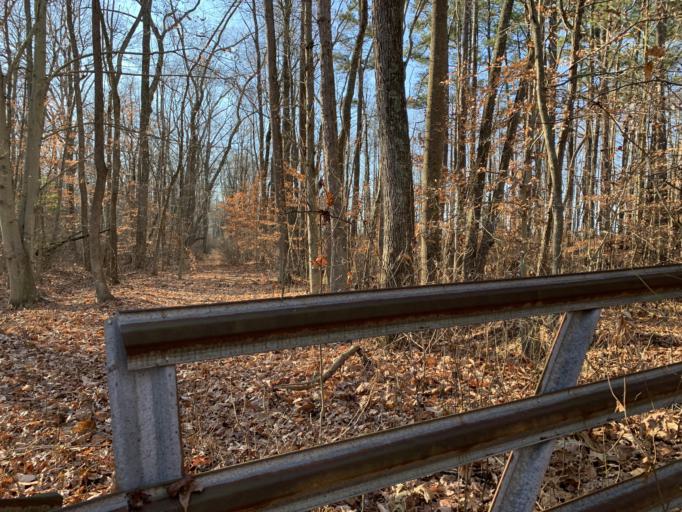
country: US
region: Delaware
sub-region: New Castle County
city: Townsend
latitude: 39.3365
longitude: -75.7386
